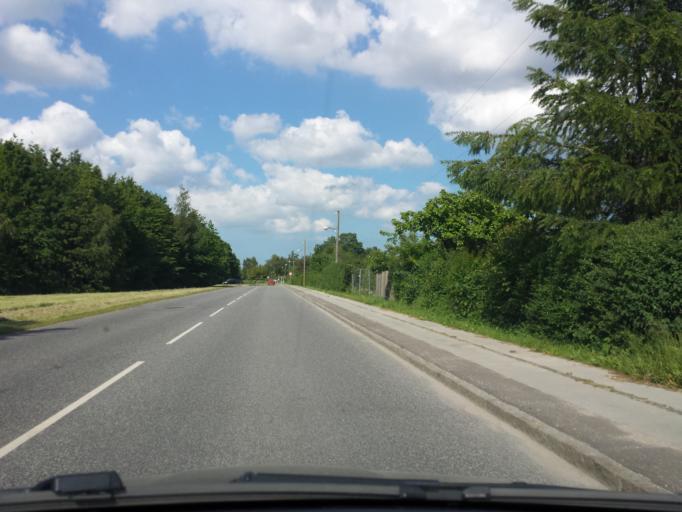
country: DK
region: Capital Region
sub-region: Ballerup Kommune
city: Ballerup
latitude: 55.7100
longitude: 12.3800
